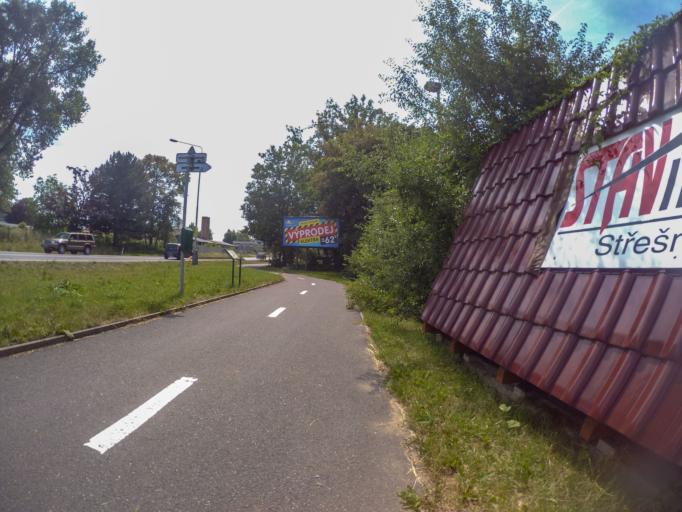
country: CZ
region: Praha
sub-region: Praha 19
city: Kbely
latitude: 50.1284
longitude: 14.5413
